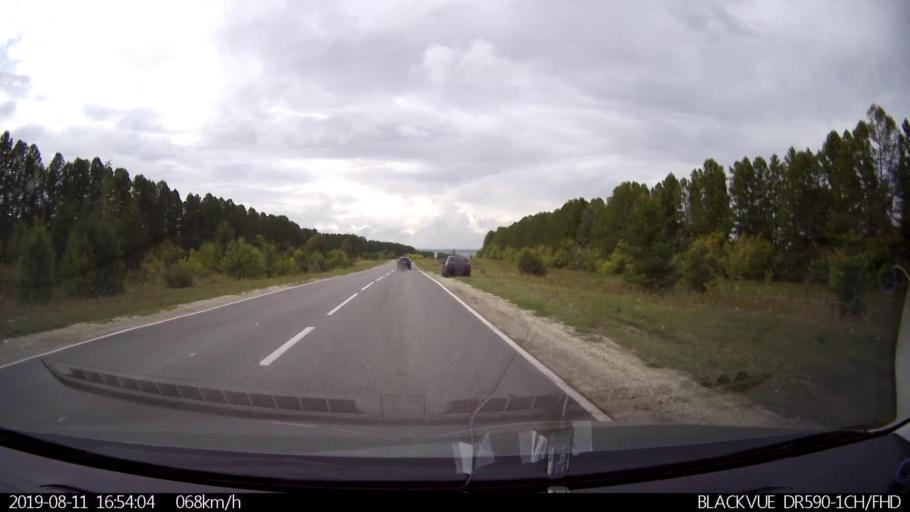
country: RU
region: Ulyanovsk
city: Mayna
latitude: 54.2689
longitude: 47.6675
